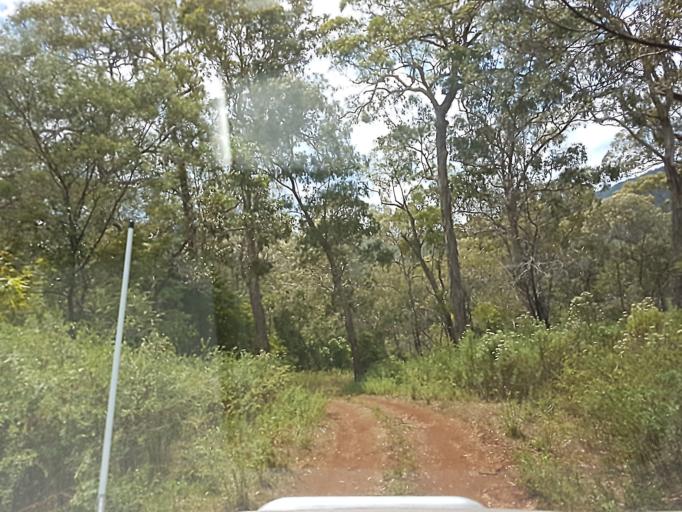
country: AU
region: Victoria
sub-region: East Gippsland
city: Lakes Entrance
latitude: -37.3572
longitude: 148.3565
